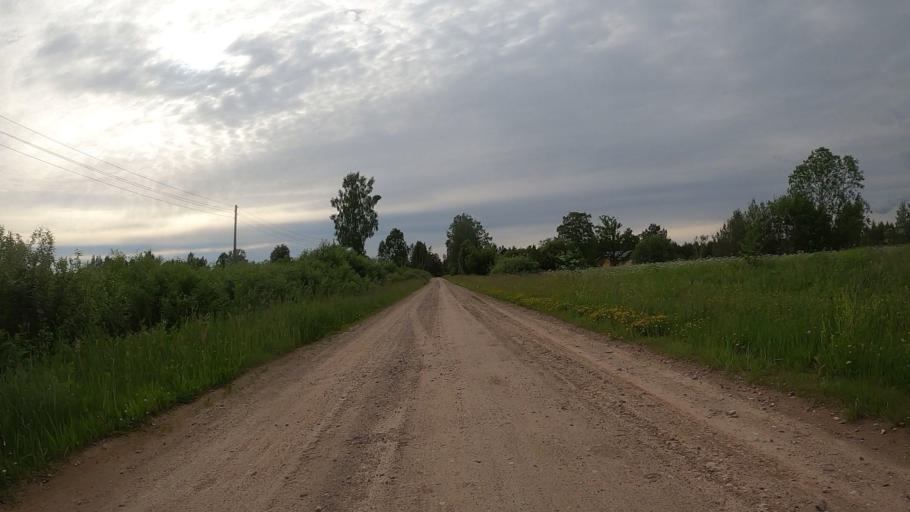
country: LV
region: Ozolnieku
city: Ozolnieki
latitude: 56.7143
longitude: 23.7911
